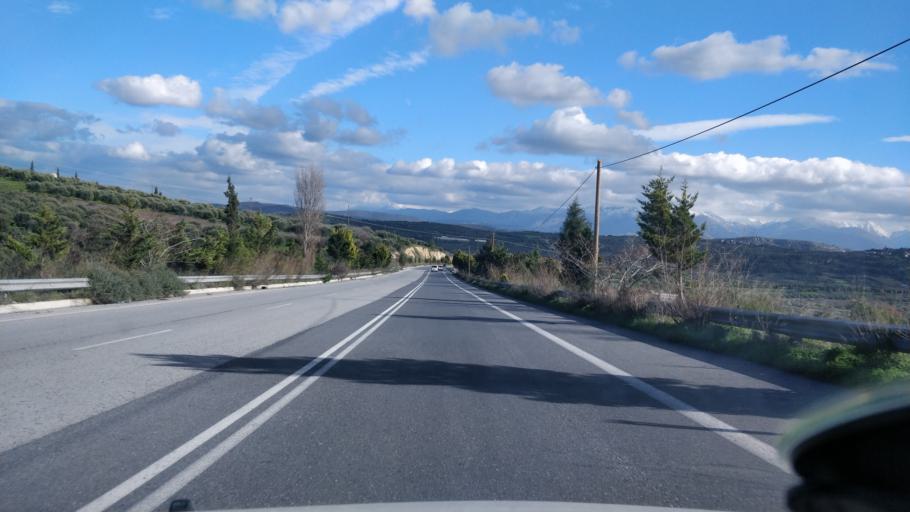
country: GR
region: Crete
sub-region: Nomos Irakleiou
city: Ano Arhanes
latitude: 35.2246
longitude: 25.1859
